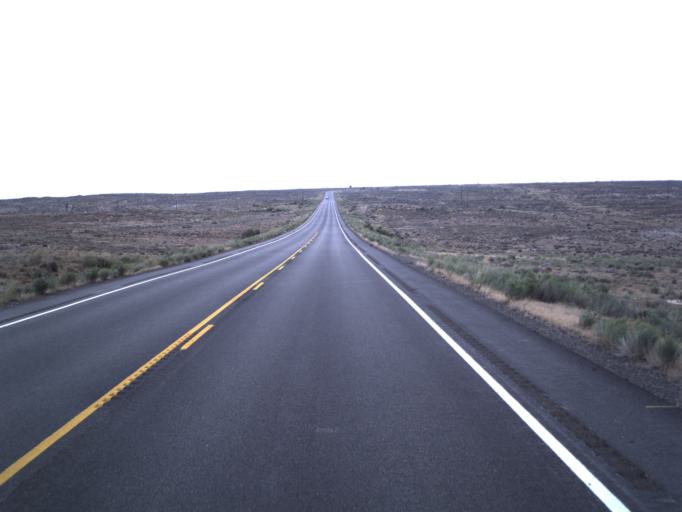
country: US
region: Utah
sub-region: Uintah County
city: Naples
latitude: 40.2121
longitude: -109.3774
